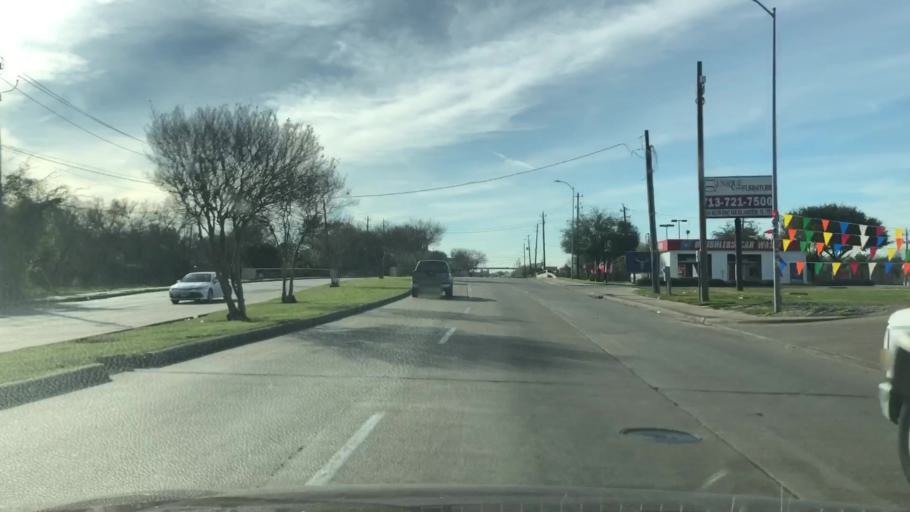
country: US
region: Texas
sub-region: Harris County
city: Bellaire
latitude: 29.6615
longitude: -95.4642
